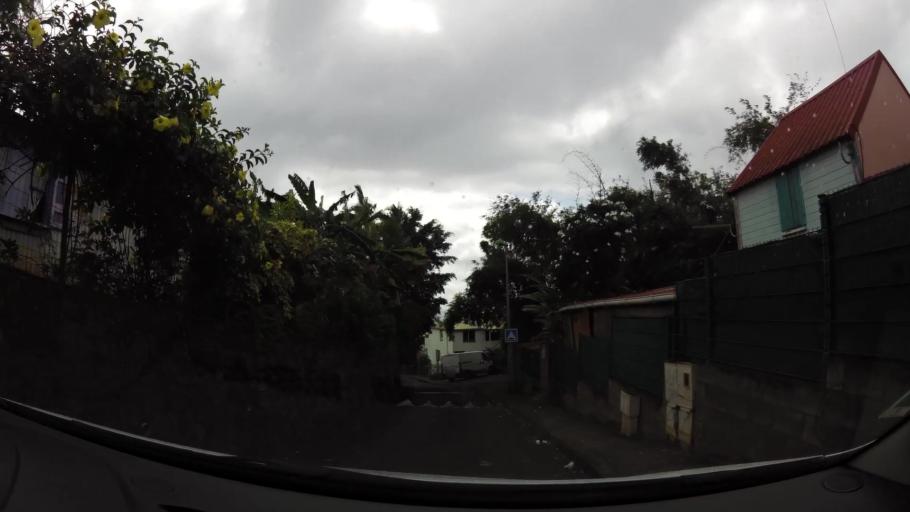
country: RE
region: Reunion
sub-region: Reunion
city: Sainte-Marie
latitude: -20.9009
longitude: 55.5496
